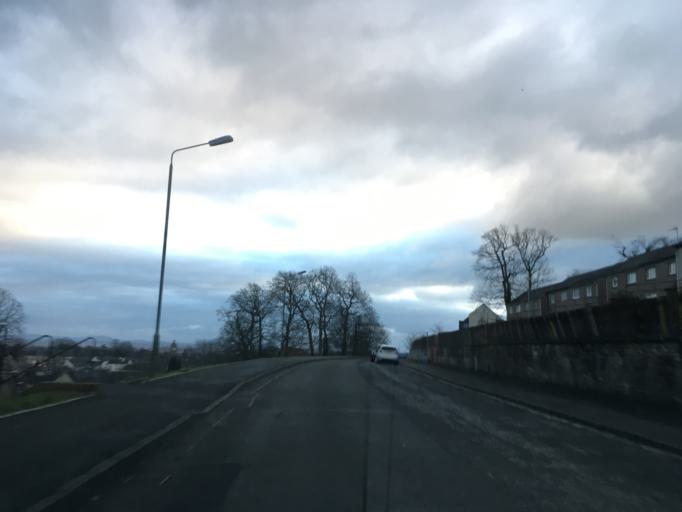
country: GB
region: Scotland
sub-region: Stirling
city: Stirling
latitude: 56.1028
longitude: -3.9475
